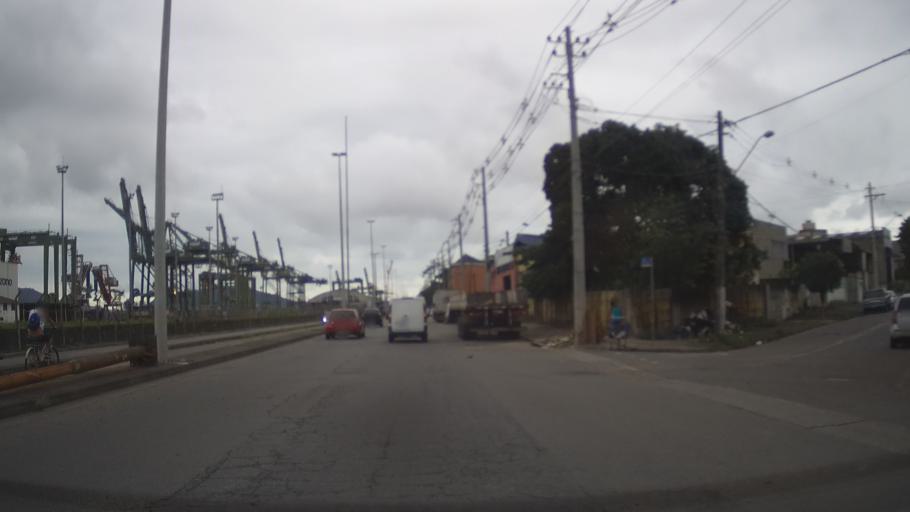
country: BR
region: Sao Paulo
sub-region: Santos
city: Santos
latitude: -23.9667
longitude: -46.3017
